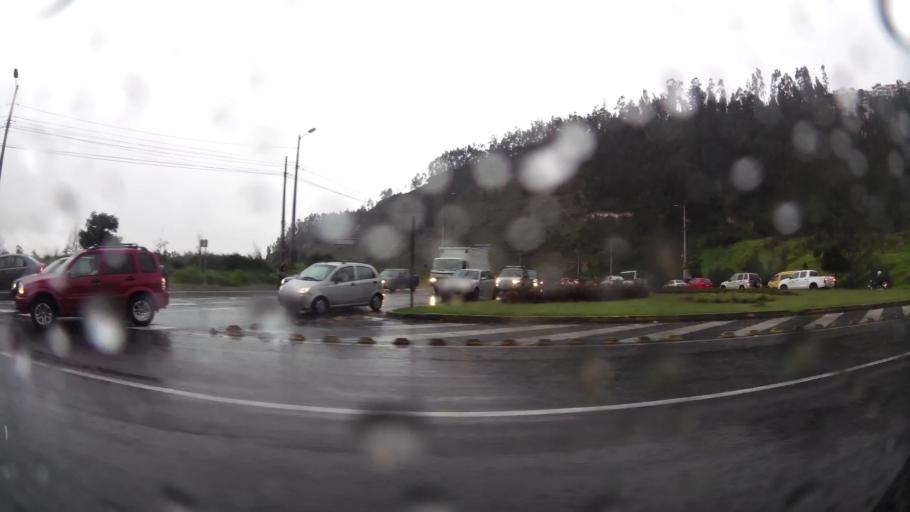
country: EC
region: Pichincha
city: Quito
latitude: -0.1506
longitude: -78.4524
